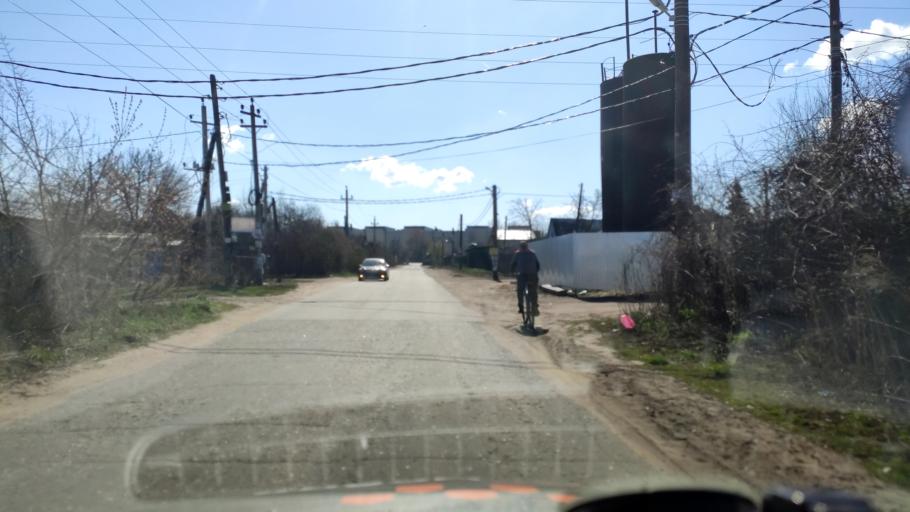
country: RU
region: Voronezj
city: Maslovka
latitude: 51.5869
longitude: 39.1672
